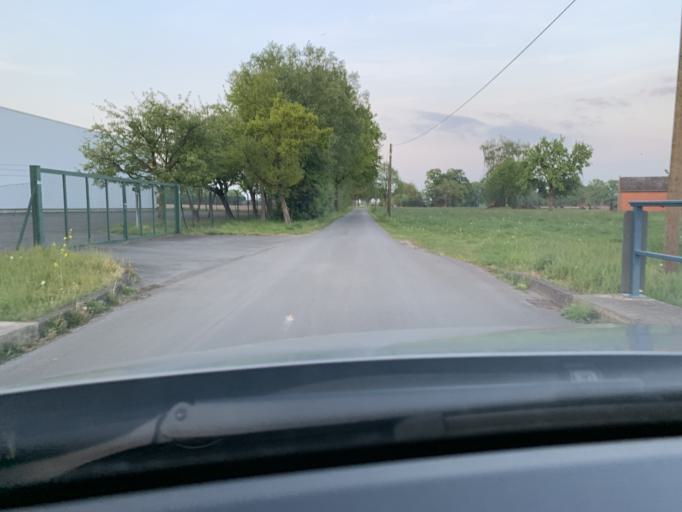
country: DE
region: North Rhine-Westphalia
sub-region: Regierungsbezirk Detmold
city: Langenberg
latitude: 51.7961
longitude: 8.3702
